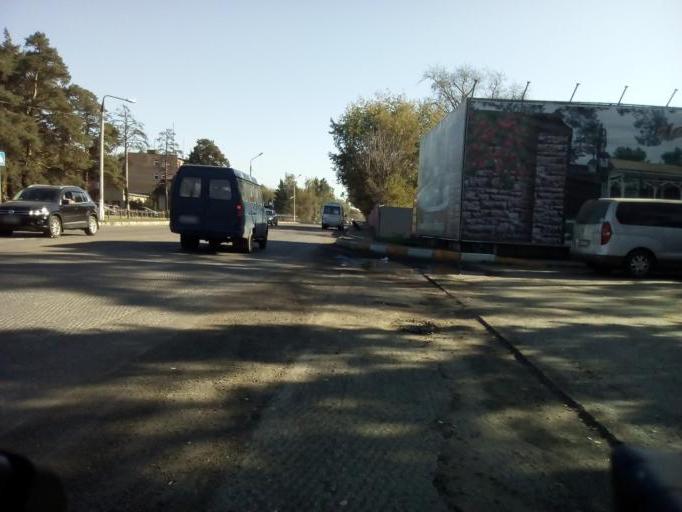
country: RU
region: Moskovskaya
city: Ramenskoye
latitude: 55.5589
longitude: 38.2548
